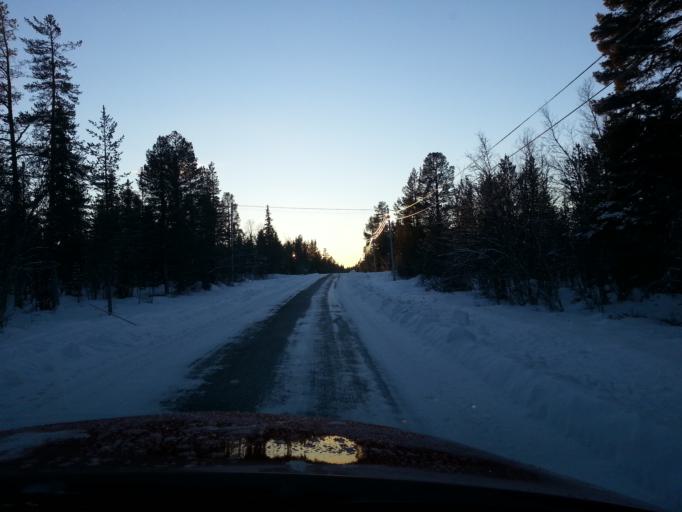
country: SE
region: Jaemtland
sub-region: Harjedalens Kommun
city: Sveg
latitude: 62.3203
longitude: 13.4185
